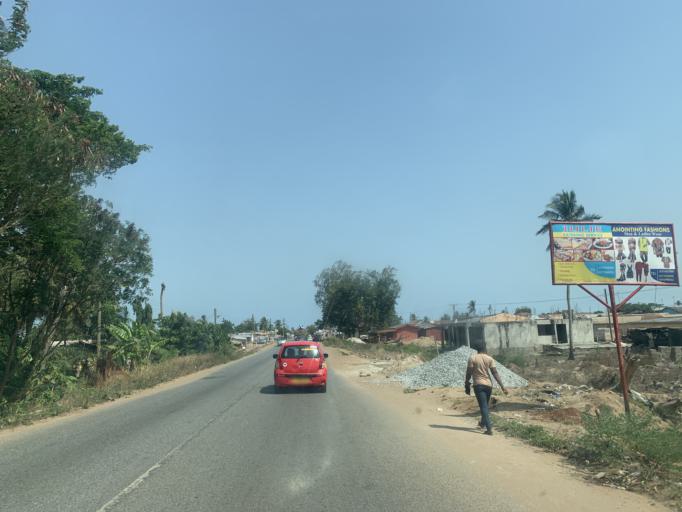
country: GH
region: Central
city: Winneba
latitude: 5.3951
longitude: -0.6482
